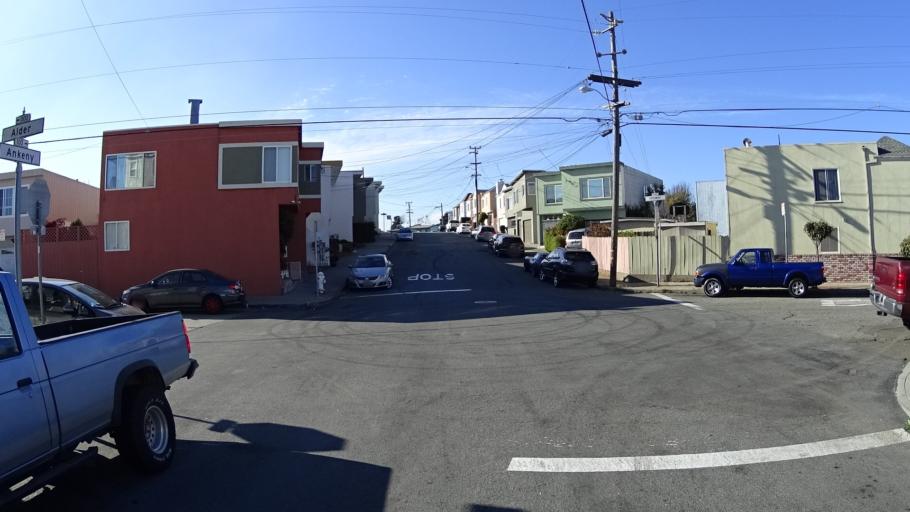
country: US
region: California
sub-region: San Mateo County
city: Brisbane
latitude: 37.7192
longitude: -122.4047
